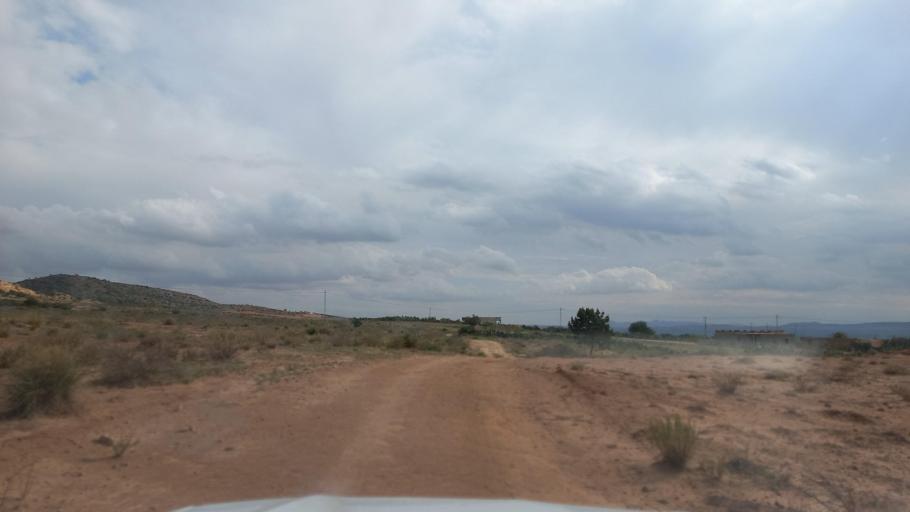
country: TN
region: Al Qasrayn
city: Sbiba
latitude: 35.2985
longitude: 9.1203
